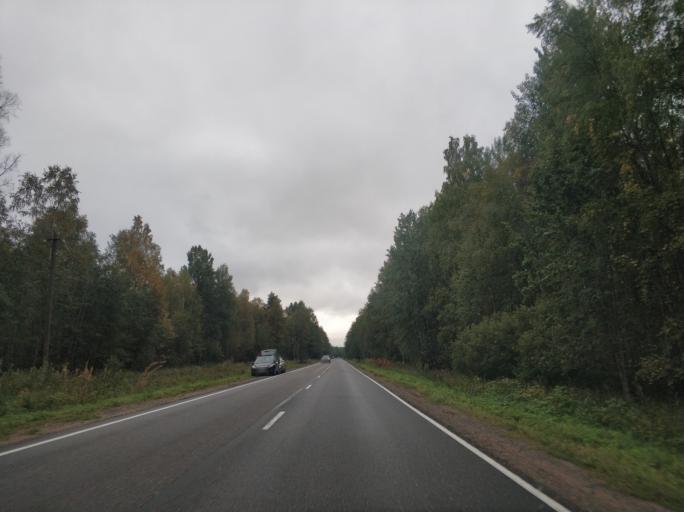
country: RU
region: Leningrad
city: Borisova Griva
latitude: 60.1239
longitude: 30.9633
